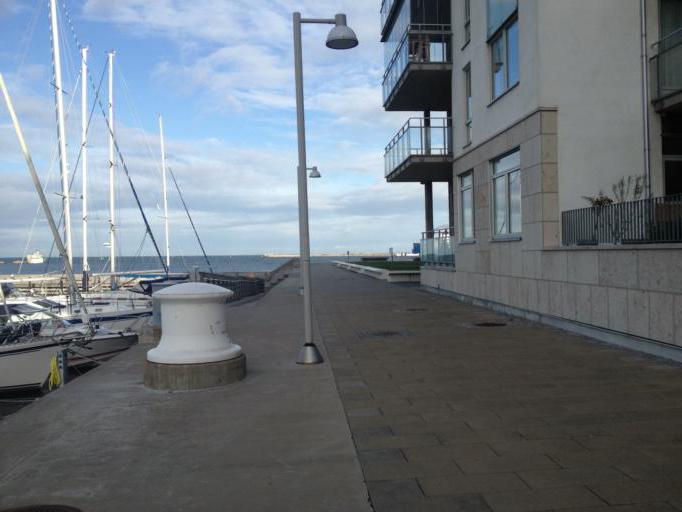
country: SE
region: Skane
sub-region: Malmo
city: Malmoe
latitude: 55.6182
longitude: 12.9889
